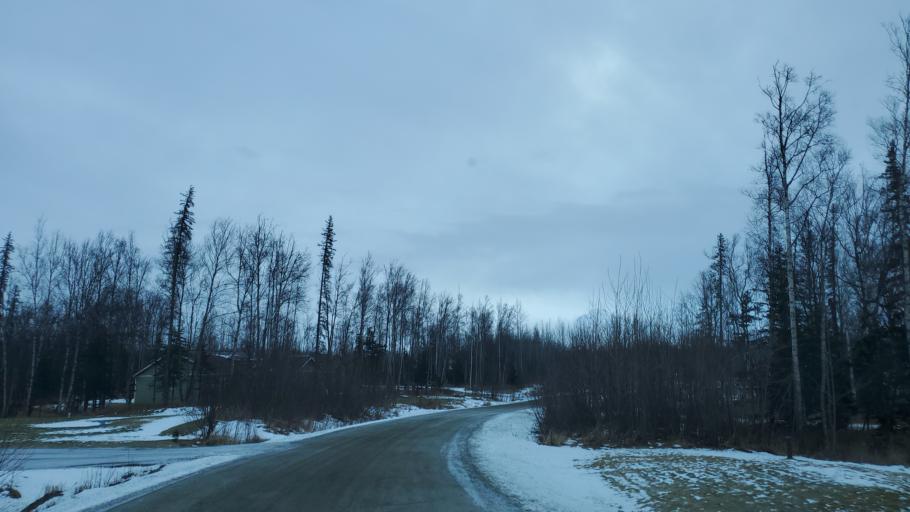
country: US
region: Alaska
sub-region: Matanuska-Susitna Borough
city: Farm Loop
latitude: 61.6563
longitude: -149.2222
